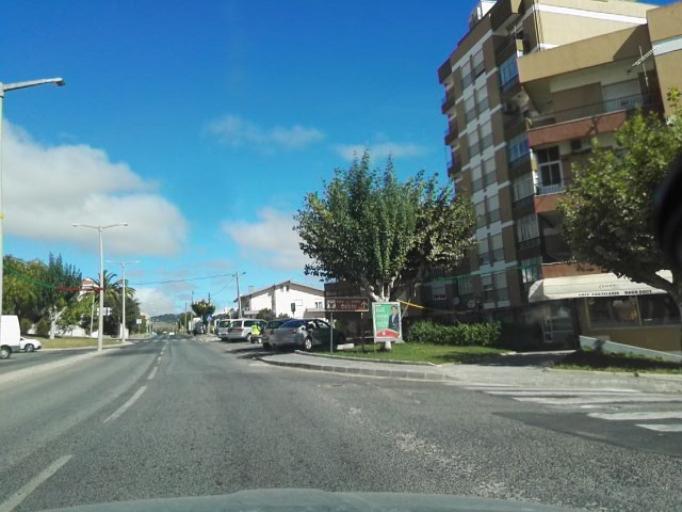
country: PT
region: Lisbon
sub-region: Arruda Dos Vinhos
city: Arruda dos Vinhos
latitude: 38.9882
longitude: -9.0789
